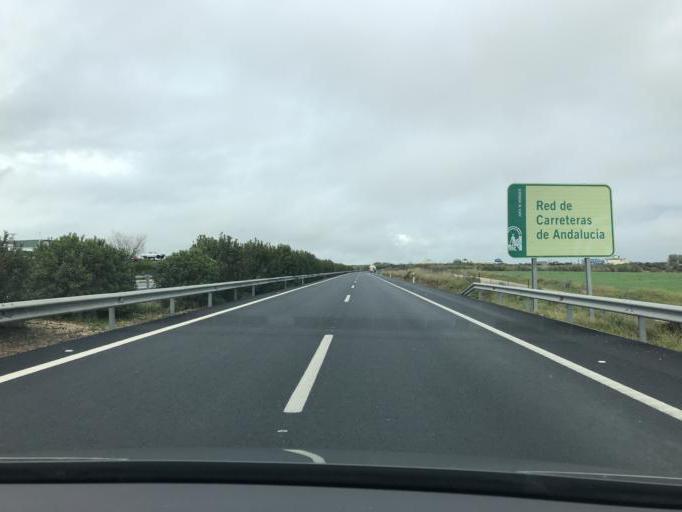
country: ES
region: Andalusia
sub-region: Provincia de Sevilla
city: Paradas
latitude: 37.2667
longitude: -5.5121
